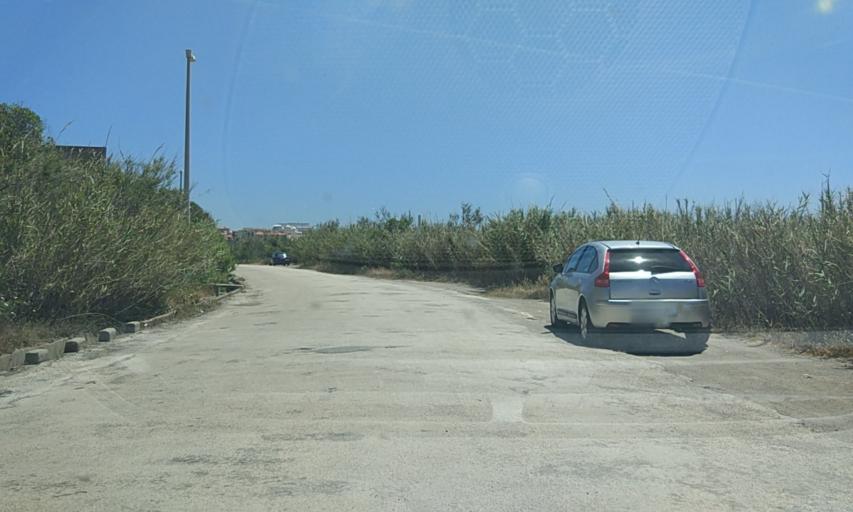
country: PT
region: Coimbra
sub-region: Figueira da Foz
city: Buarcos
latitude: 40.1783
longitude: -8.9049
